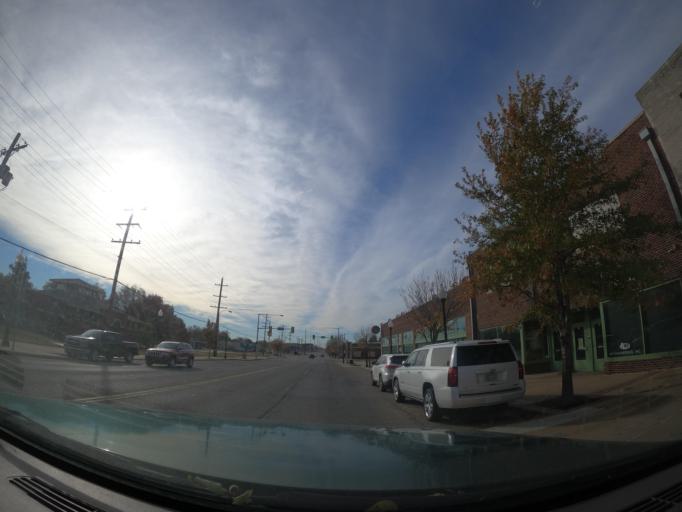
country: US
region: Oklahoma
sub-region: Tulsa County
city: Tulsa
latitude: 36.1593
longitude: -95.9582
